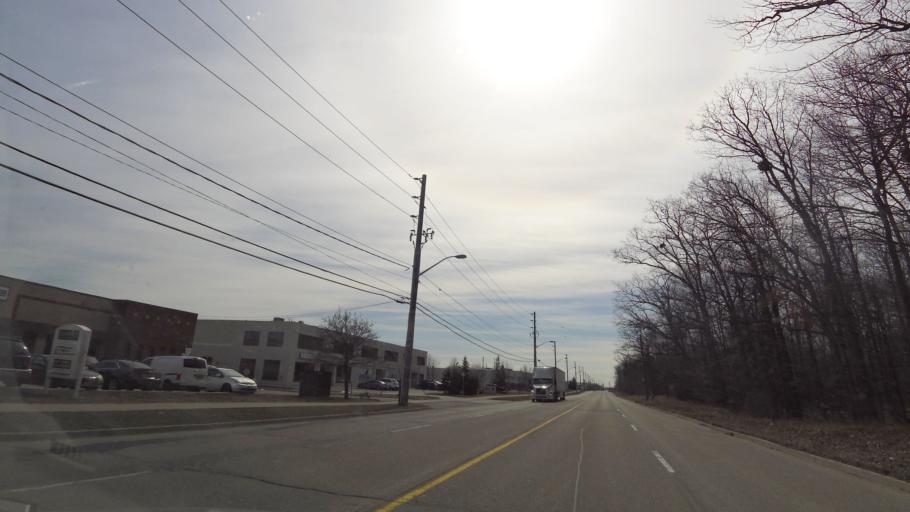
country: CA
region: Ontario
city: Burlington
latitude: 43.3995
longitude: -79.7678
